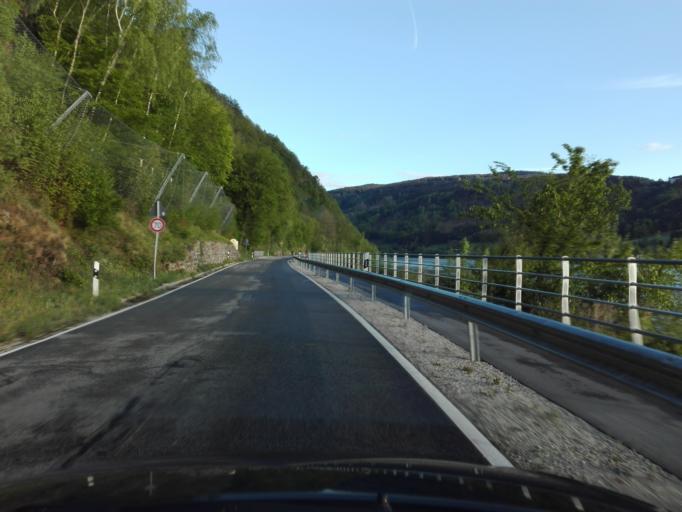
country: DE
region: Bavaria
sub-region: Lower Bavaria
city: Obernzell
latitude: 48.5475
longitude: 13.6566
